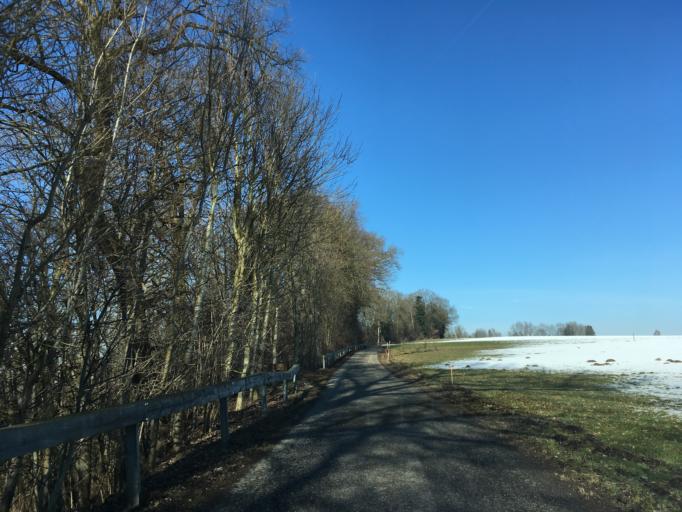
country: DE
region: Bavaria
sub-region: Upper Bavaria
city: Griesstatt
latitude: 47.9704
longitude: 12.1595
